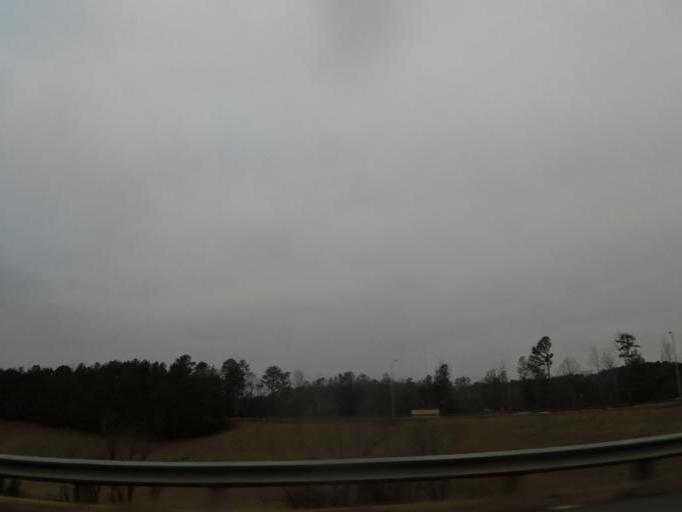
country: US
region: Alabama
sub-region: Cullman County
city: Good Hope
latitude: 34.0770
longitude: -86.8665
